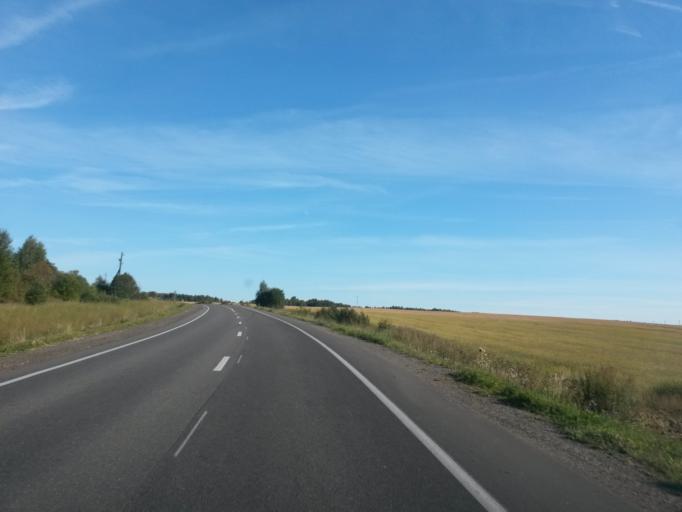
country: RU
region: Jaroslavl
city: Gavrilov-Yam
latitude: 57.3271
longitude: 39.9222
